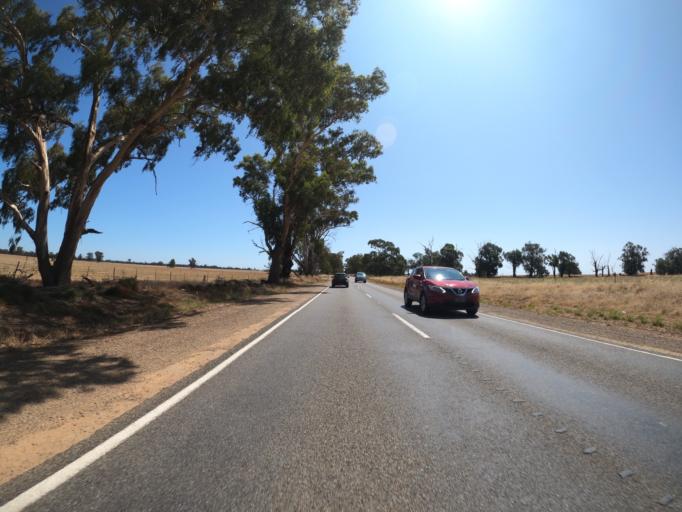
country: AU
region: Victoria
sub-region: Moira
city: Yarrawonga
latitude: -36.0244
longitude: 146.1090
